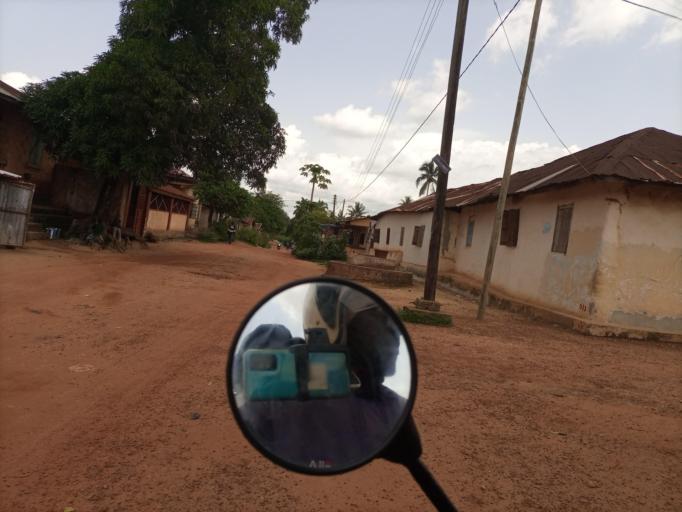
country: SL
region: Southern Province
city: Bo
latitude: 7.9571
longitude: -11.7356
